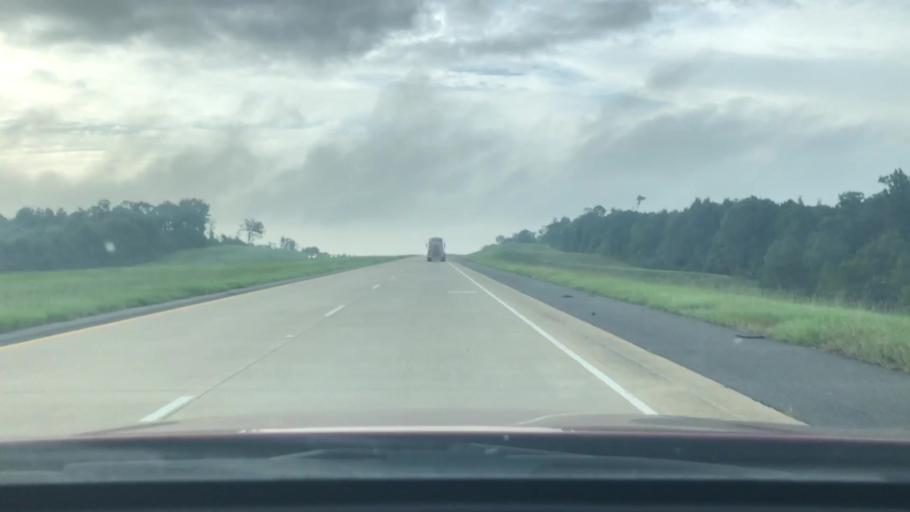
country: US
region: Louisiana
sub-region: Caddo Parish
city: Vivian
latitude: 32.9642
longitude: -93.9048
